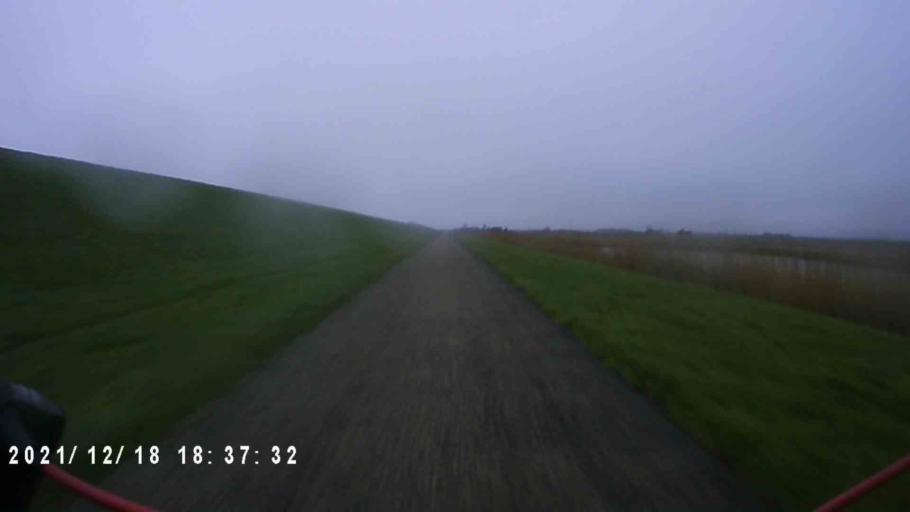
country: NL
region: Friesland
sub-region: Gemeente Dongeradeel
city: Ternaard
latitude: 53.4037
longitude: 6.0443
